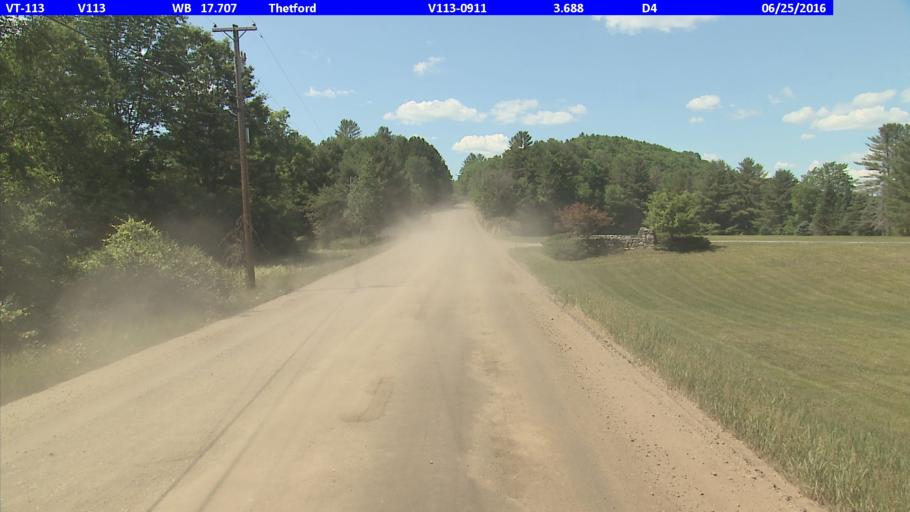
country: US
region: New Hampshire
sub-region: Grafton County
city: Lyme
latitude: 43.8471
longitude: -72.2531
